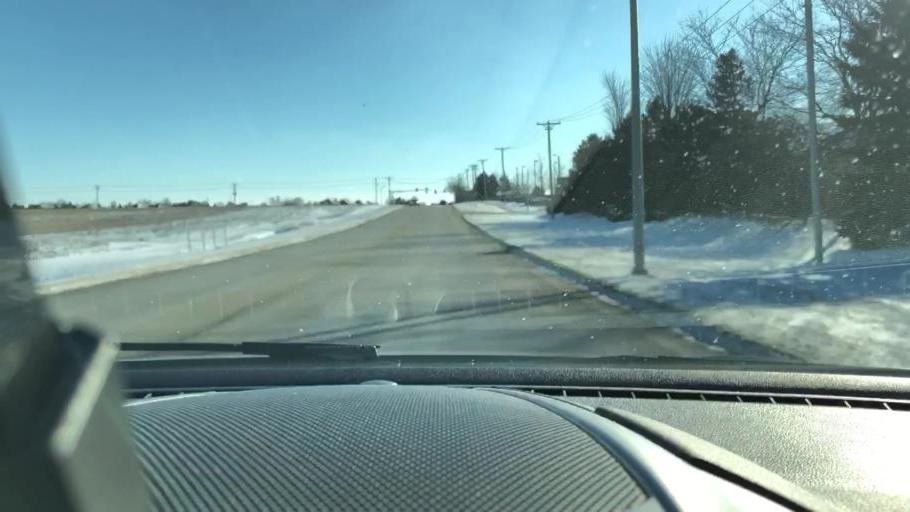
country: US
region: Illinois
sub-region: Will County
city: Mokena
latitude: 41.4870
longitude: -87.8879
